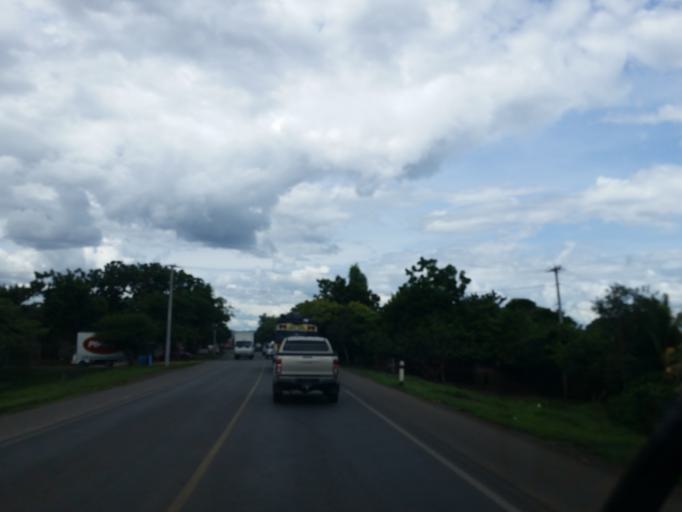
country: NI
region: Managua
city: Tipitapa
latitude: 12.2866
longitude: -86.0593
